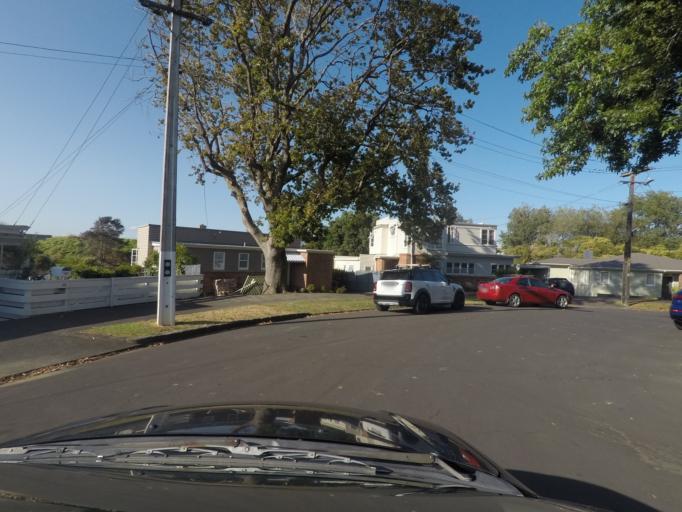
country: NZ
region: Auckland
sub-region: Auckland
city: Rosebank
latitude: -36.8631
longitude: 174.7132
